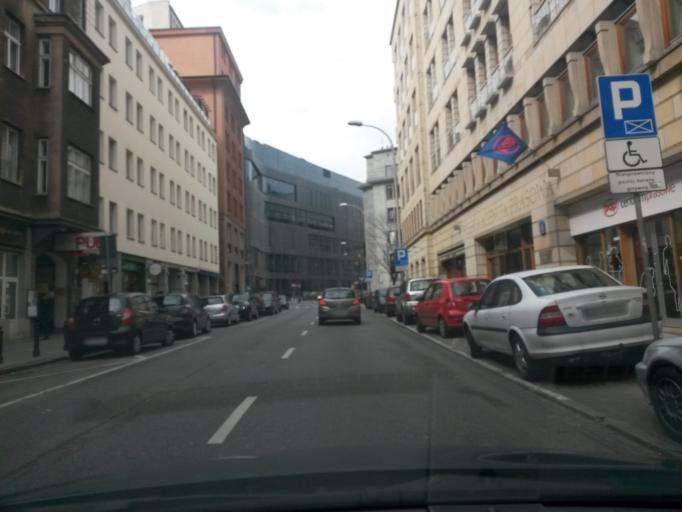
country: PL
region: Masovian Voivodeship
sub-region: Warszawa
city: Srodmiescie
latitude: 52.2299
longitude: 21.0204
